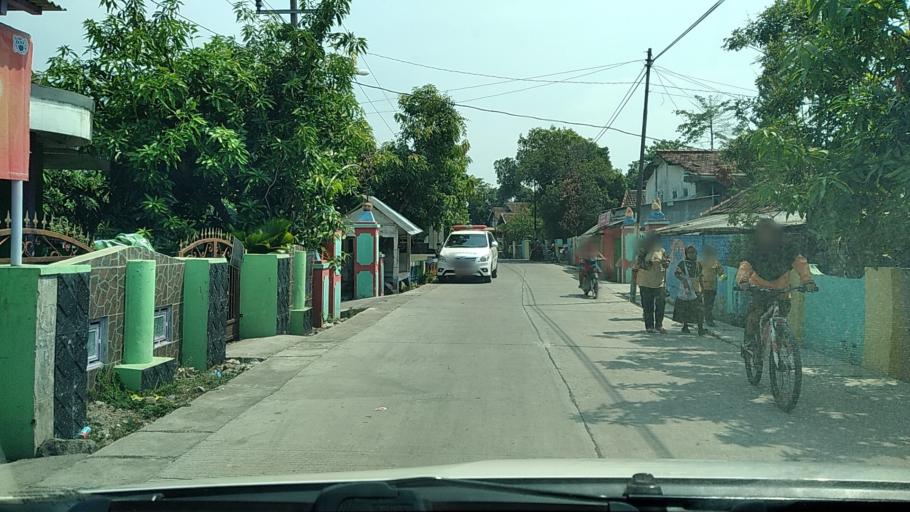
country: ID
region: Central Java
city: Semarang
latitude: -6.9735
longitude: 110.3445
